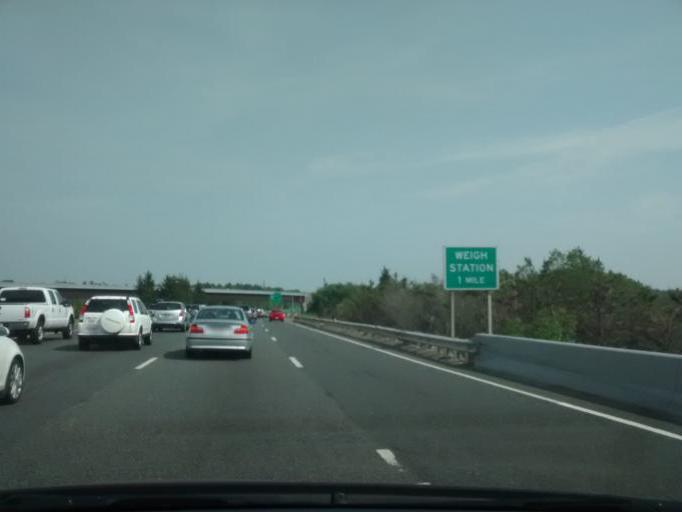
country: US
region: Massachusetts
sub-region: Bristol County
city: Raynham Center
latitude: 41.9481
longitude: -71.0231
